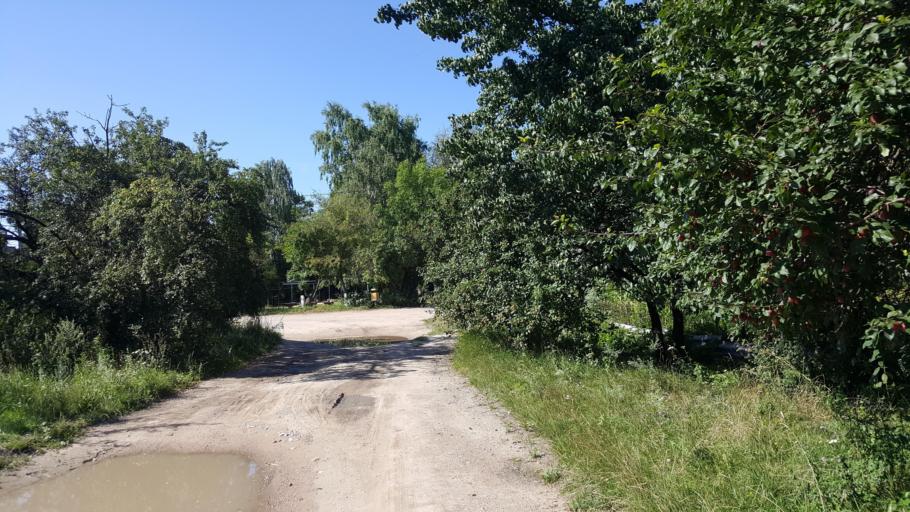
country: BY
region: Brest
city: Charnawchytsy
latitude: 52.2096
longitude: 23.7393
